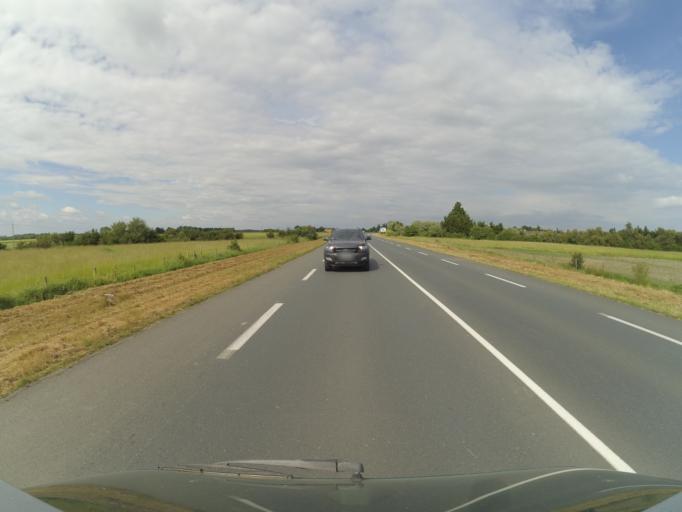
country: FR
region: Pays de la Loire
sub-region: Departement de la Vendee
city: Champagne-les-Marais
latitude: 46.4249
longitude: -1.0947
